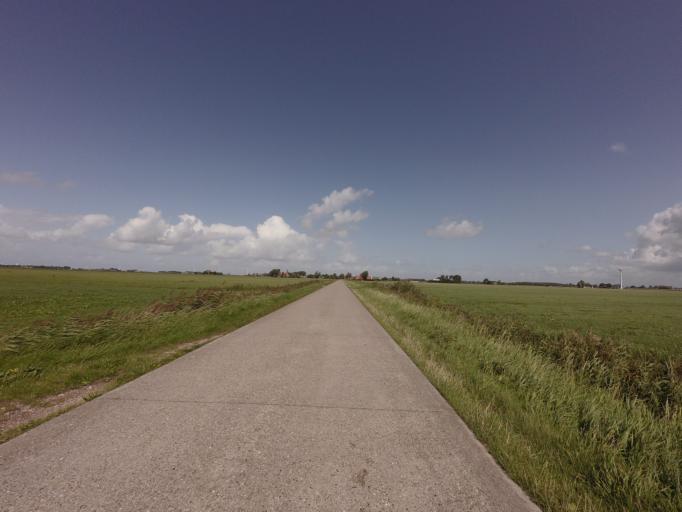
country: NL
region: Friesland
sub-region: Sudwest Fryslan
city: Makkum
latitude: 53.0720
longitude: 5.4538
